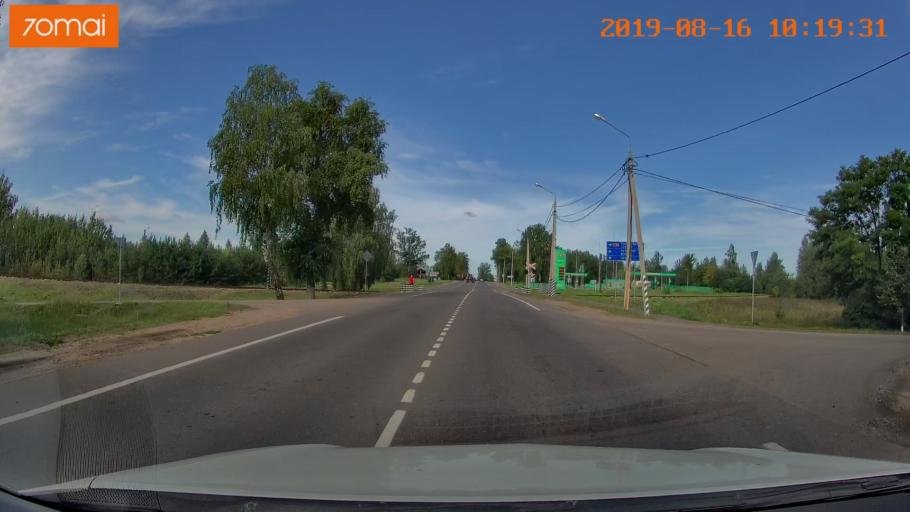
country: BY
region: Mogilev
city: Asipovichy
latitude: 53.3063
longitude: 28.6651
